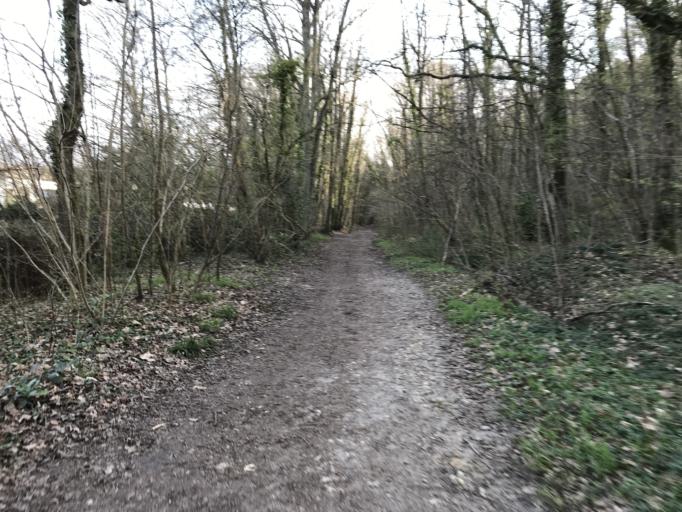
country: FR
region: Ile-de-France
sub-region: Departement des Yvelines
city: Saint-Remy-les-Chevreuse
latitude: 48.6945
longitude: 2.0593
